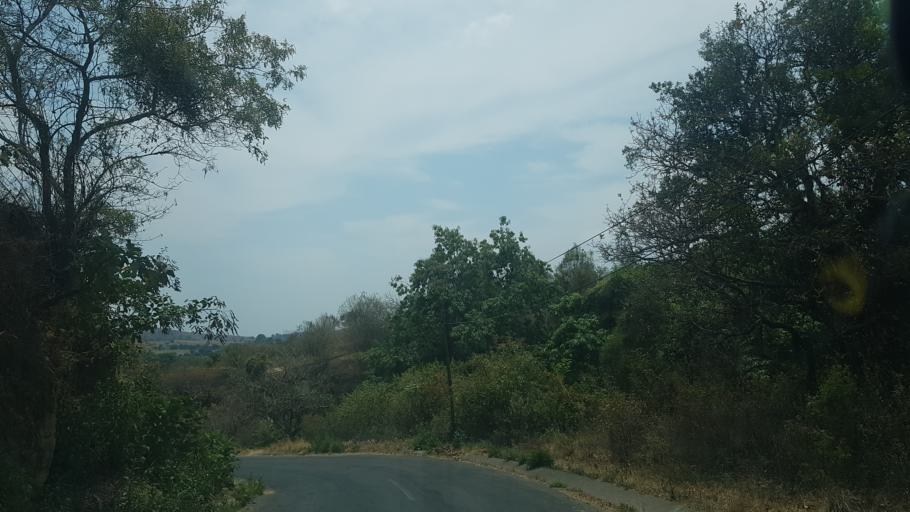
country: MX
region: Puebla
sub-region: Tochimilco
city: La Magdalena Yancuitlalpan
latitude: 18.8720
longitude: -98.6144
